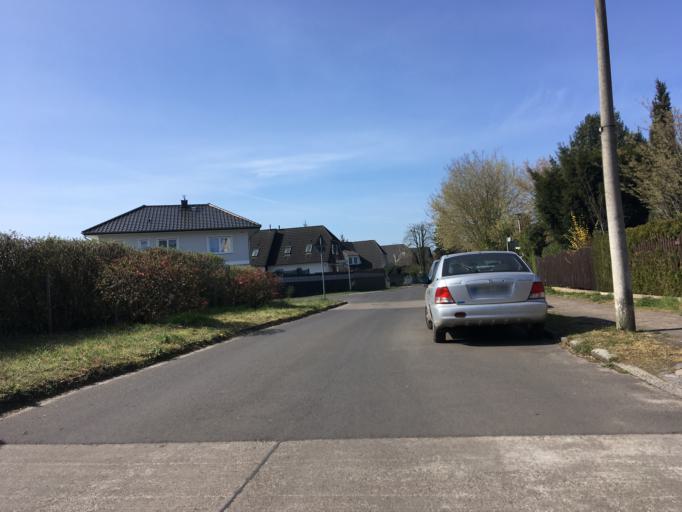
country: DE
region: Berlin
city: Kaulsdorf
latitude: 52.4950
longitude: 13.5804
